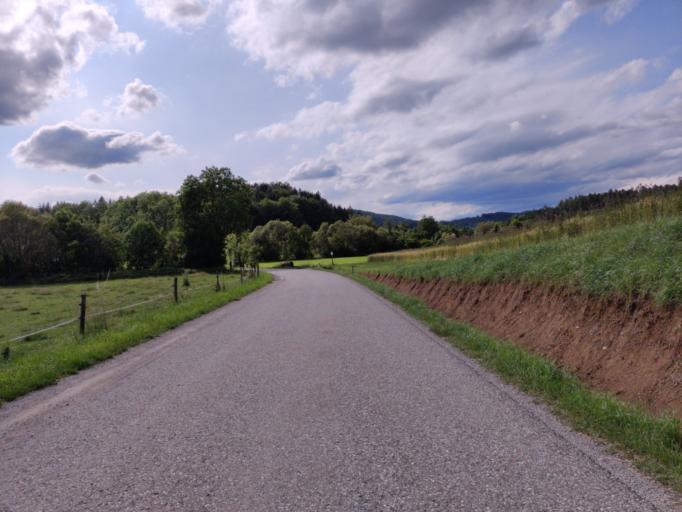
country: AT
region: Styria
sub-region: Politischer Bezirk Graz-Umgebung
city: Thal
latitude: 47.0610
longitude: 15.3486
